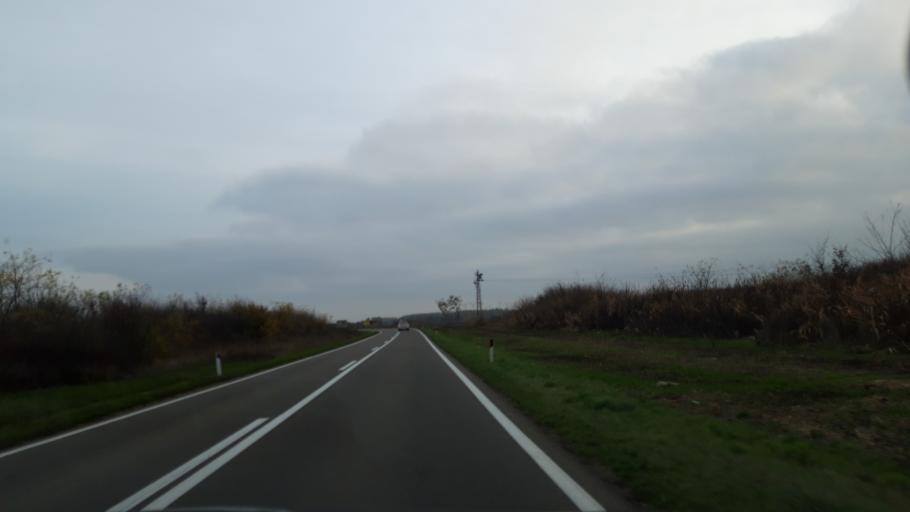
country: RS
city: Sanad
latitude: 46.0007
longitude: 20.1026
